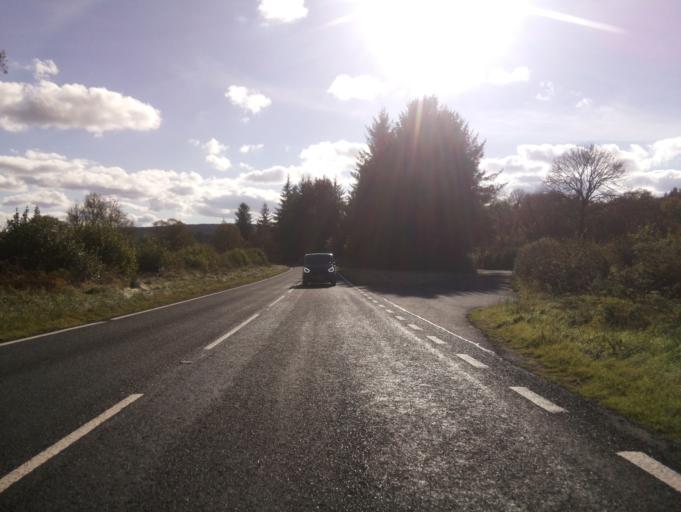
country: GB
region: Wales
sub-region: Merthyr Tydfil County Borough
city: Merthyr Tydfil
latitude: 51.8141
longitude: -3.4442
